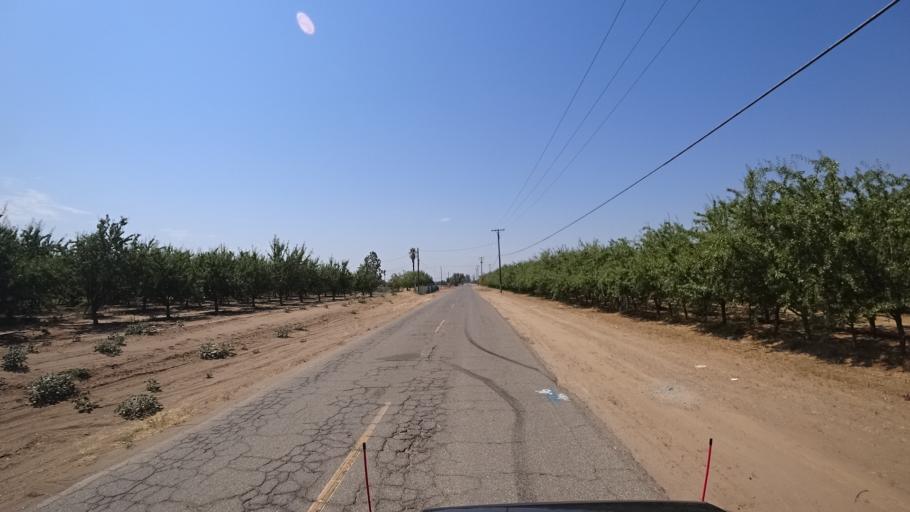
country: US
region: California
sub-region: Fresno County
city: West Park
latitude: 36.7237
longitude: -119.8357
